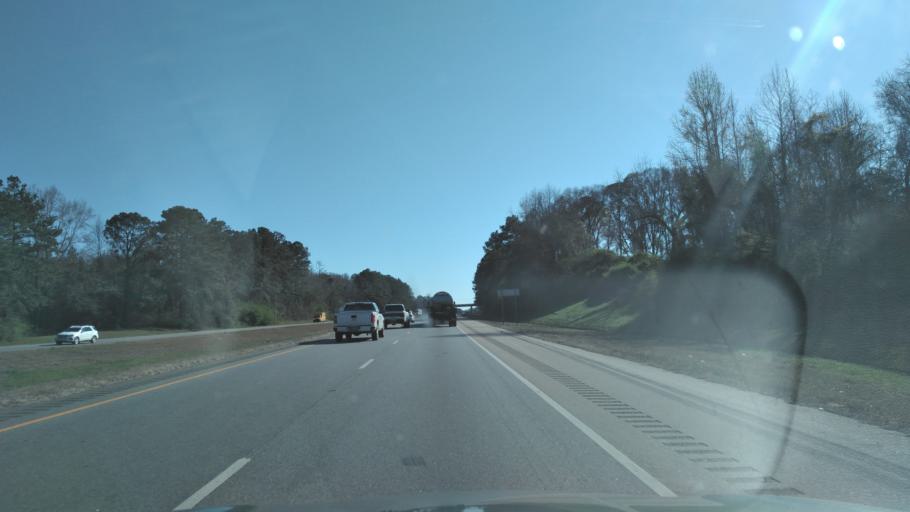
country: US
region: Alabama
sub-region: Butler County
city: Greenville
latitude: 31.8093
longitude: -86.6680
